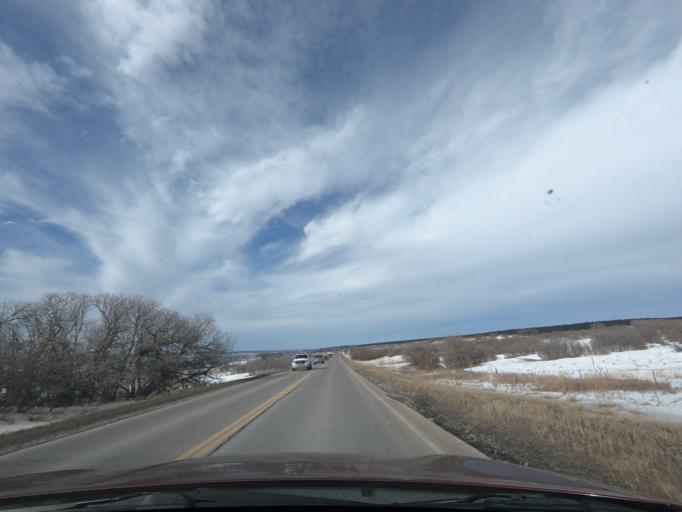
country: US
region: Colorado
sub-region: Douglas County
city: The Pinery
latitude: 39.3626
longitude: -104.7475
